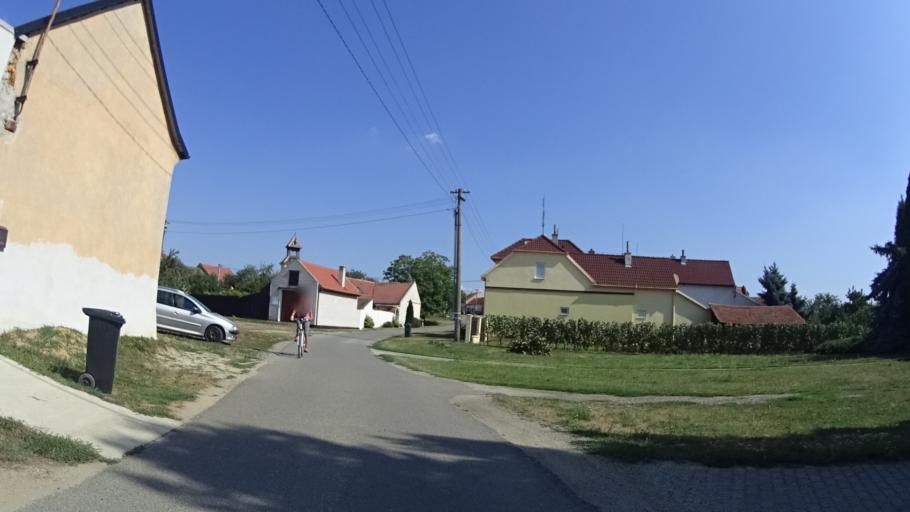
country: CZ
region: Zlin
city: Uhersky Ostroh
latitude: 48.9916
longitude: 17.4068
